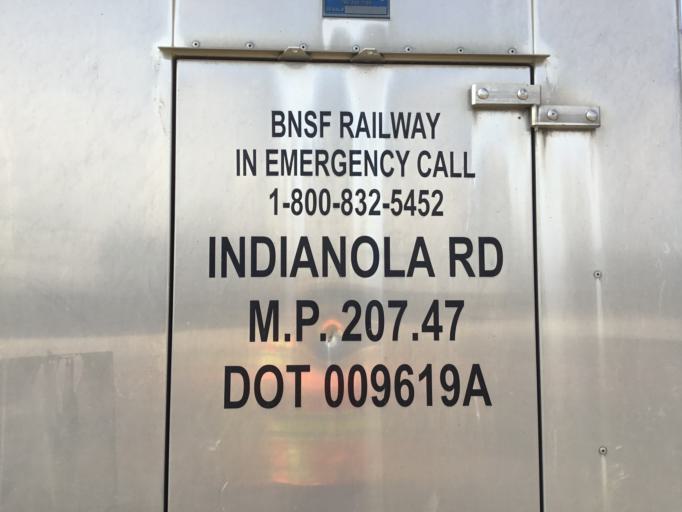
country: US
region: Kansas
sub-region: Butler County
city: Rose Hill
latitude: 37.5989
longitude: -97.0806
